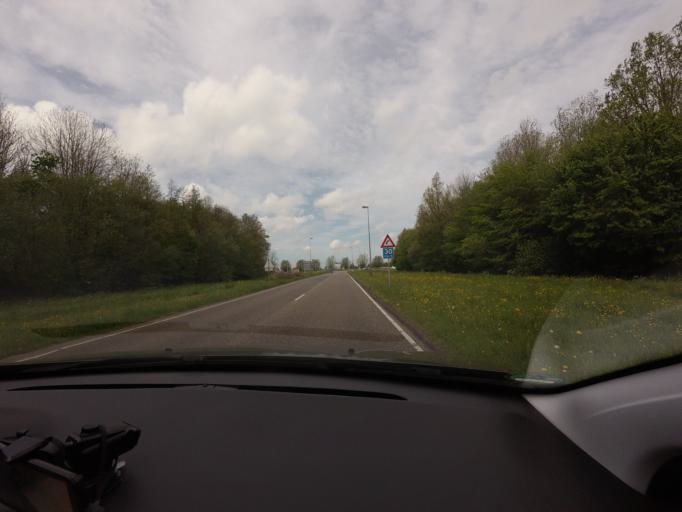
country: NL
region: North Holland
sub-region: Gemeente Beemster
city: Halfweg
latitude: 52.5065
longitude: 4.9308
